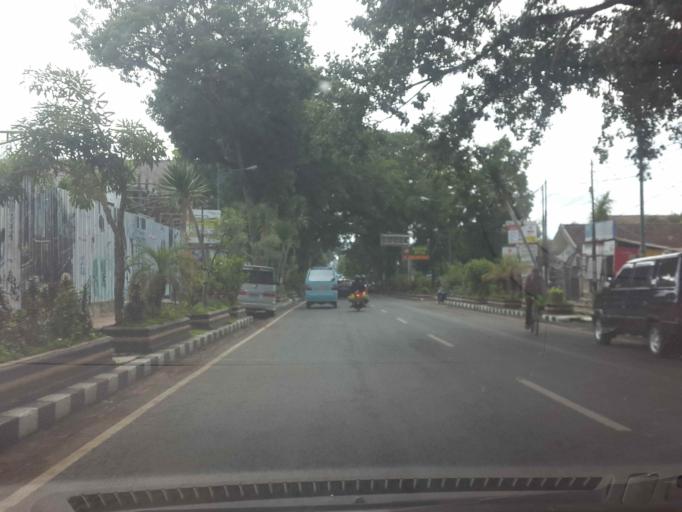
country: ID
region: Central Java
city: Salatiga
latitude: -7.3217
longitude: 110.5004
